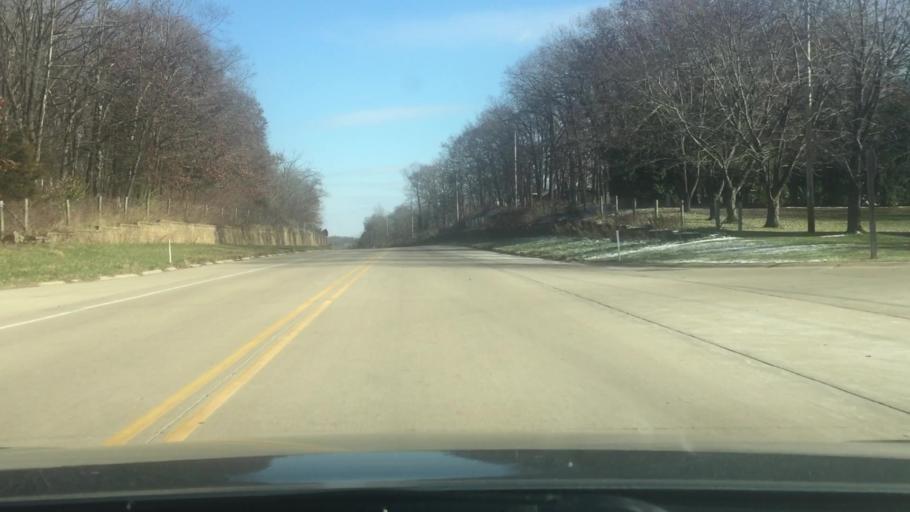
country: US
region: Wisconsin
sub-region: Jefferson County
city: Lake Ripley
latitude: 42.9736
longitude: -88.9333
